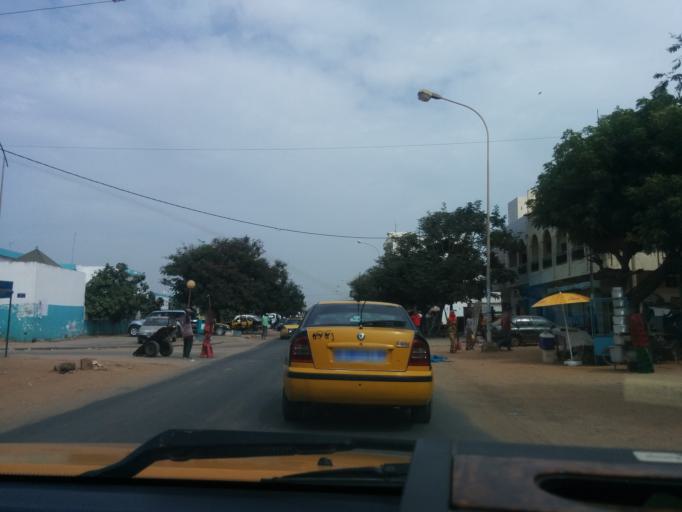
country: SN
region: Dakar
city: Grand Dakar
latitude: 14.7569
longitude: -17.4392
